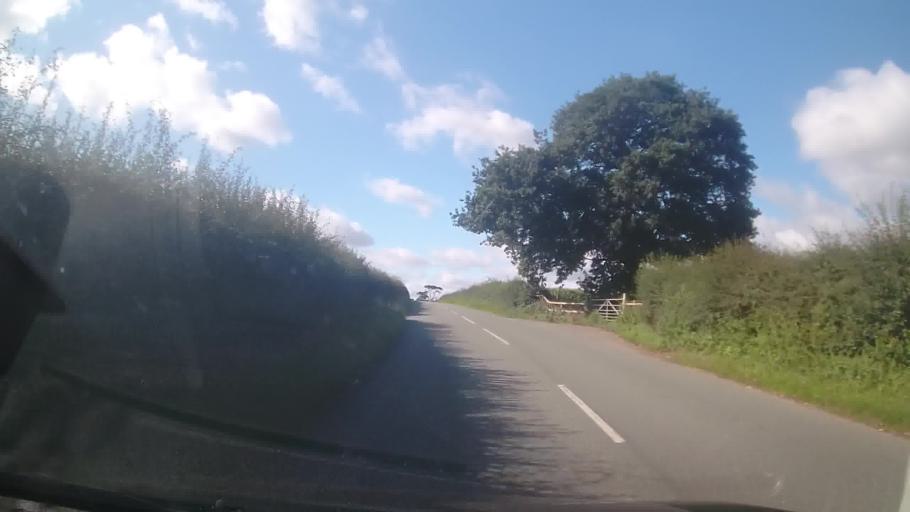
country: GB
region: England
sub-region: Shropshire
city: Ford
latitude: 52.7200
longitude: -2.8400
